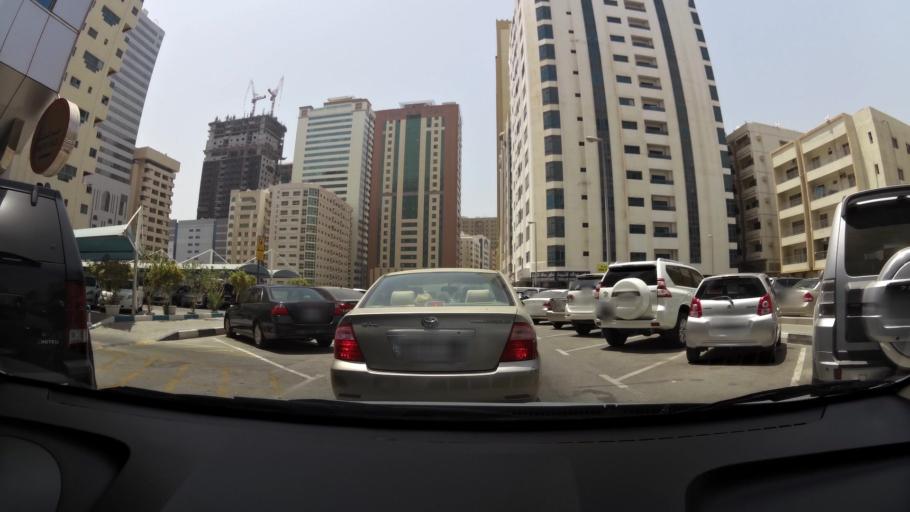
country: AE
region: Ash Shariqah
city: Sharjah
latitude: 25.3358
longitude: 55.3895
